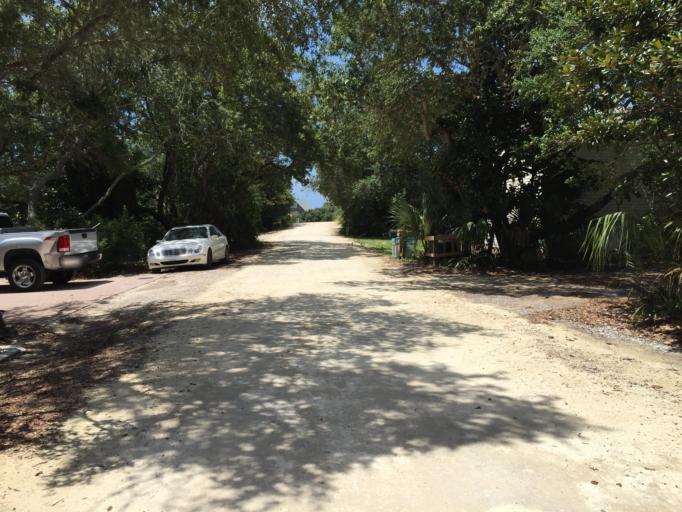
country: US
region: Florida
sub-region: Walton County
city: Seaside
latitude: 30.3093
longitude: -86.0970
